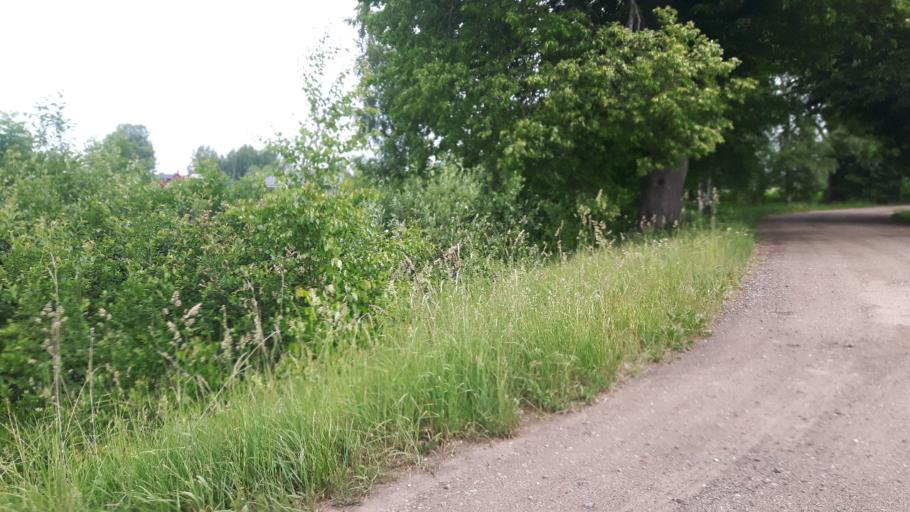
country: LV
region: Salacgrivas
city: Salacgriva
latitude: 57.6872
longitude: 24.3666
